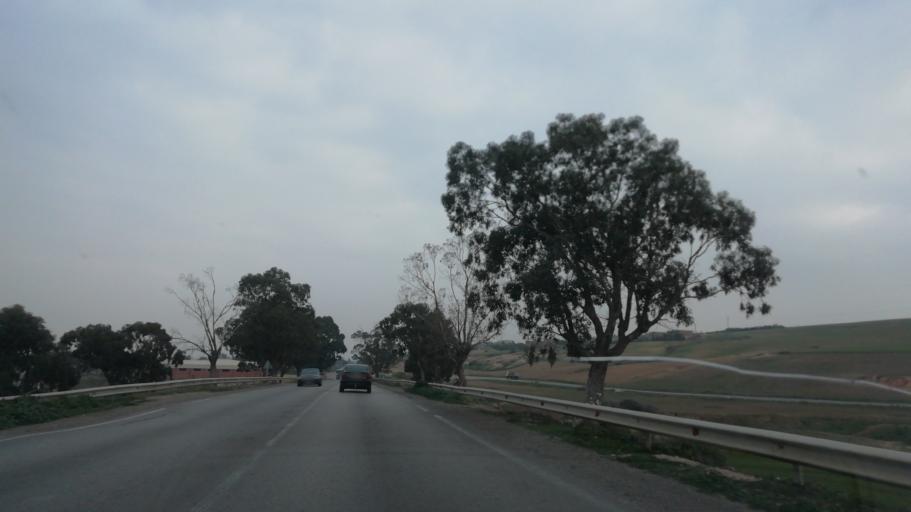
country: DZ
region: Mascara
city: Sig
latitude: 35.5538
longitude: -0.2598
